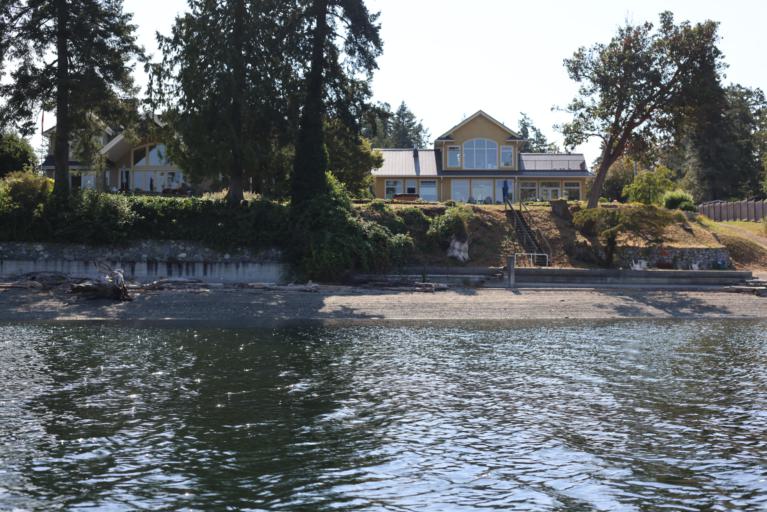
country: CA
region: British Columbia
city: North Saanich
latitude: 48.6470
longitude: -123.4612
